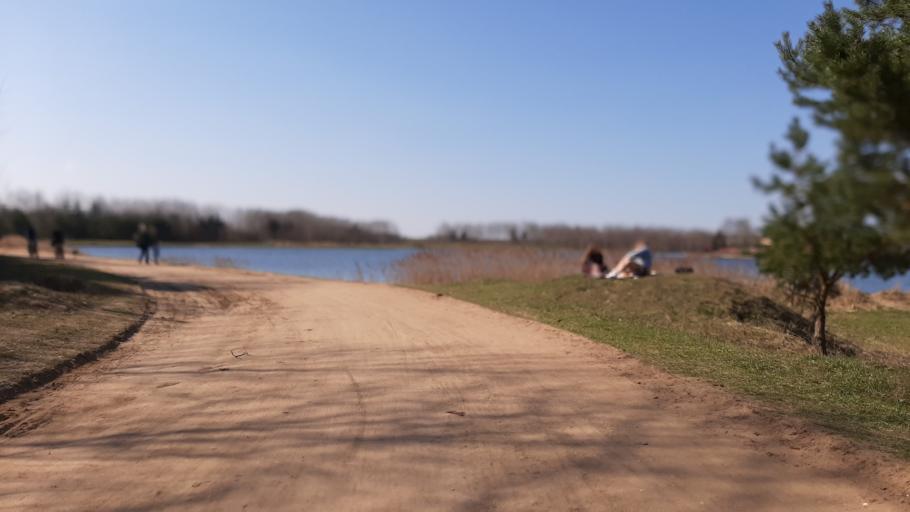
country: BY
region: Minsk
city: Bal'shavik
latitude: 53.9572
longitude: 27.5753
